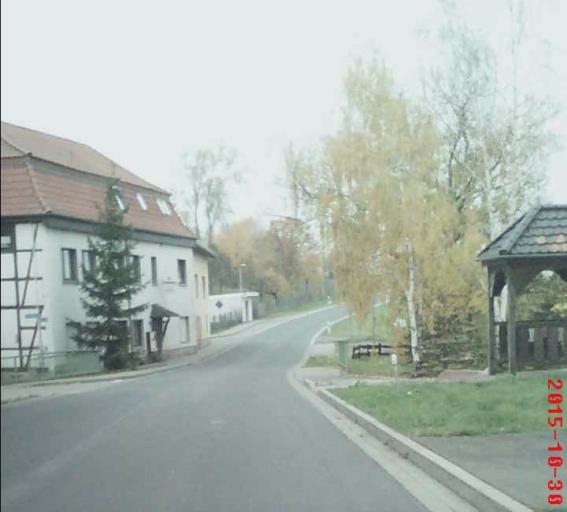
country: DE
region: Thuringia
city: Anrode
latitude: 51.2396
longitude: 10.3749
